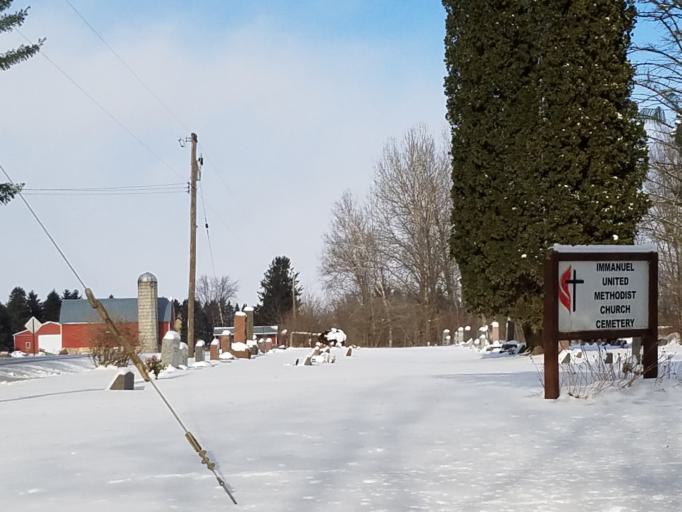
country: US
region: Wisconsin
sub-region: Marathon County
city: Spencer
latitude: 44.6127
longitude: -90.3764
